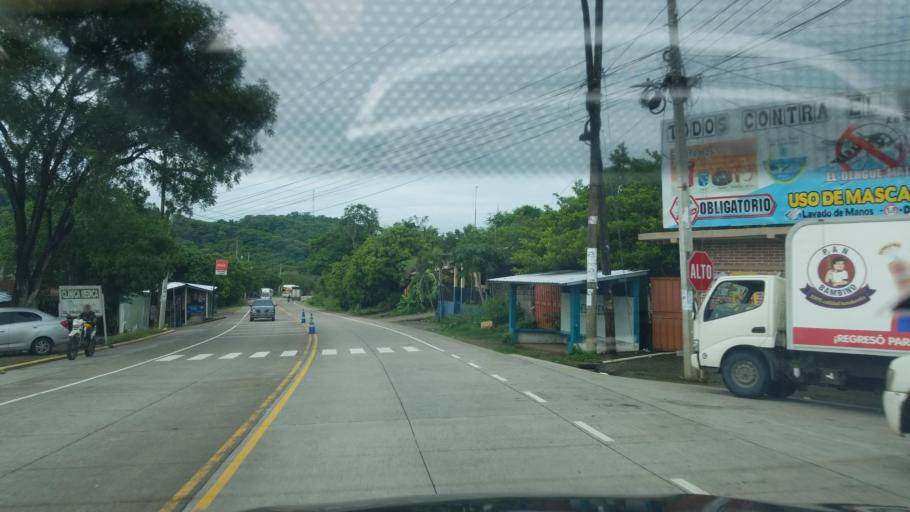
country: HN
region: Choluteca
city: Pespire
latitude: 13.6659
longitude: -87.3607
